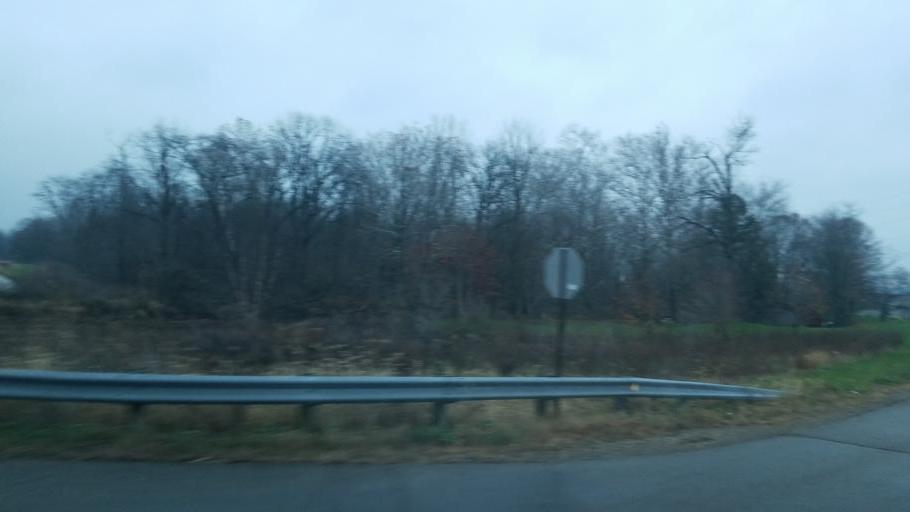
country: US
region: Ohio
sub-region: Knox County
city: Fredericktown
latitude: 40.4388
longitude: -82.5382
